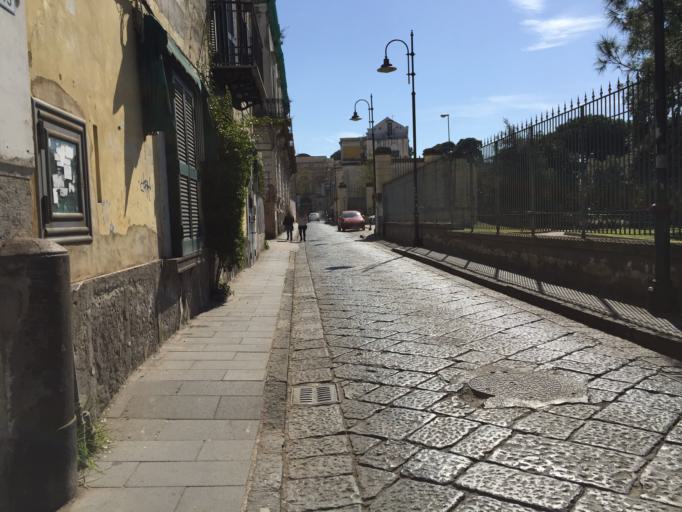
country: IT
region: Campania
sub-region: Provincia di Napoli
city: San Giorgio a Cremano
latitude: 40.8294
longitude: 14.3390
